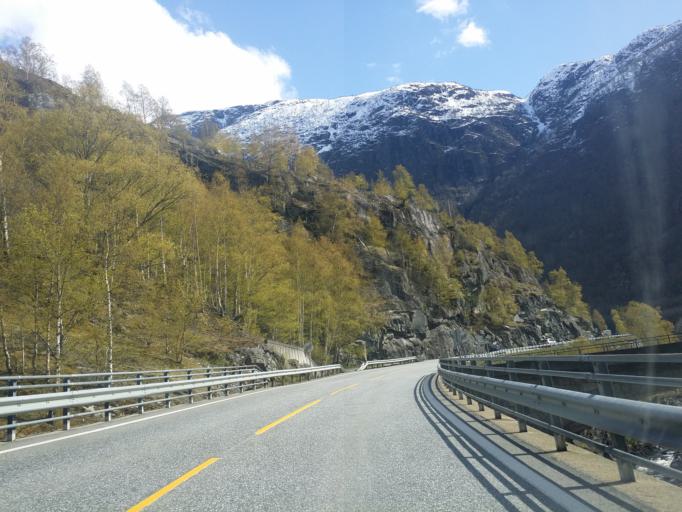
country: NO
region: Hordaland
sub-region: Eidfjord
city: Eidfjord
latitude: 60.4220
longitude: 7.1409
